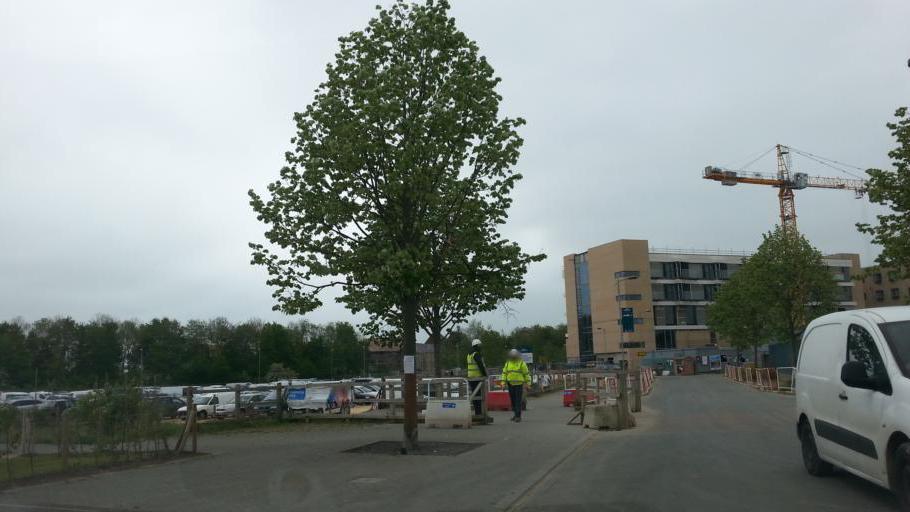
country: GB
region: England
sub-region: Cambridgeshire
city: Cambridge
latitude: 52.1747
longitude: 0.1228
